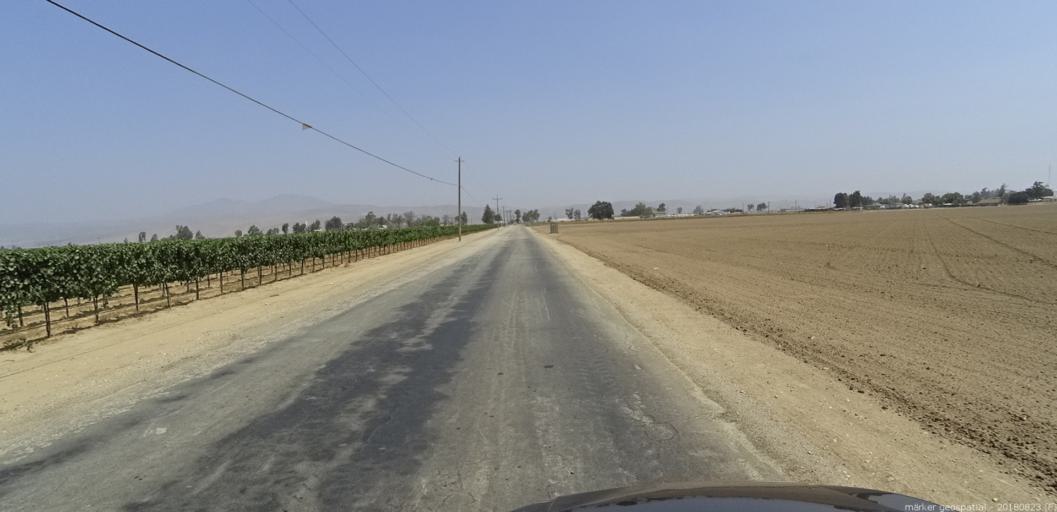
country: US
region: California
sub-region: Monterey County
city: Greenfield
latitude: 36.3333
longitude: -121.2606
